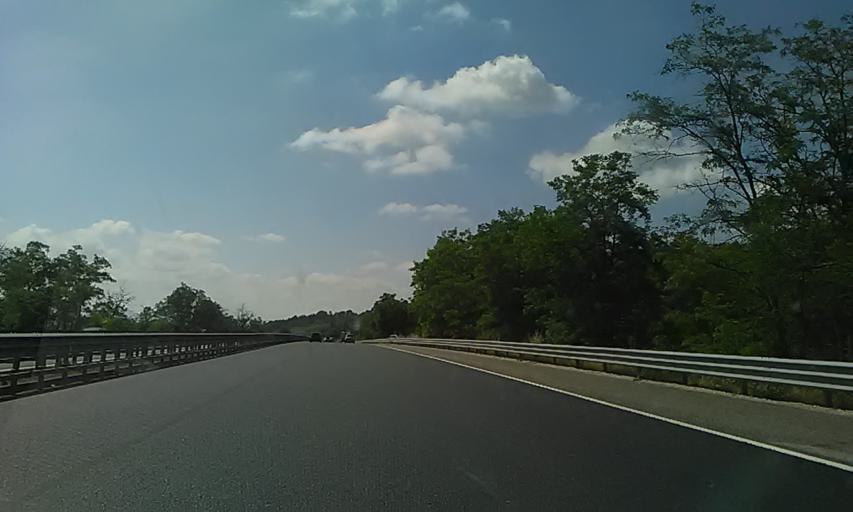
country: IT
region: Piedmont
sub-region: Provincia di Alessandria
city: Predosa
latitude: 44.7466
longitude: 8.6479
